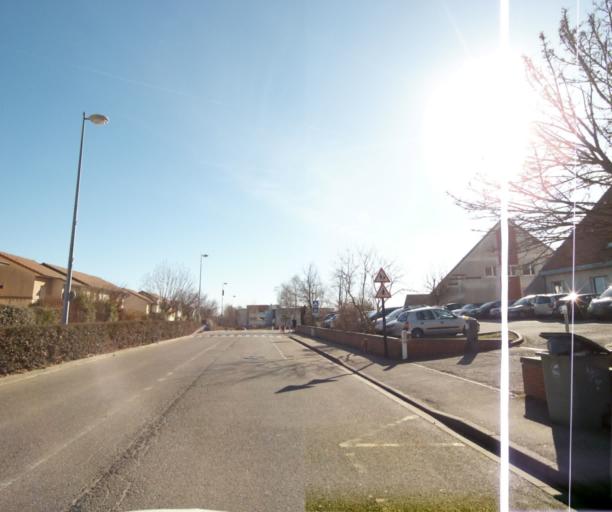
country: FR
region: Lorraine
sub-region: Departement de Meurthe-et-Moselle
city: Ludres
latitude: 48.6201
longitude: 6.1689
